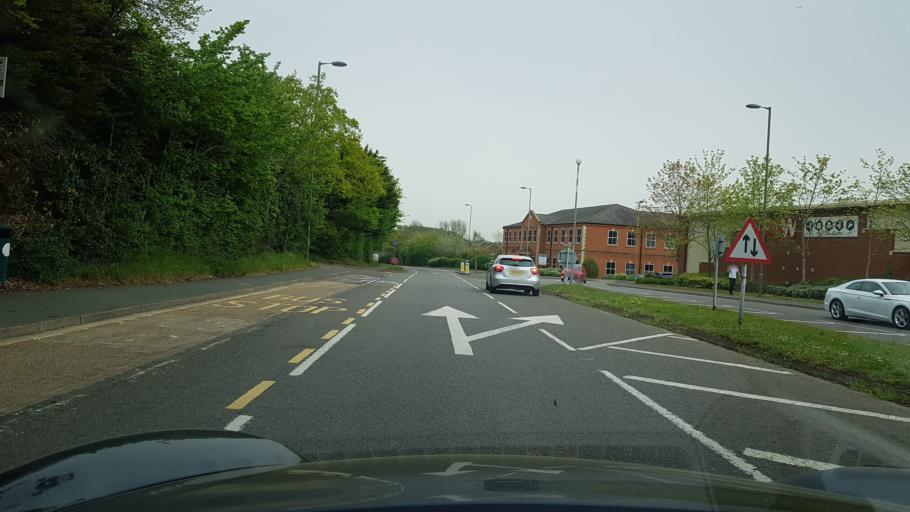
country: GB
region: England
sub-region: Surrey
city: Send
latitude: 51.2821
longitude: -0.5138
